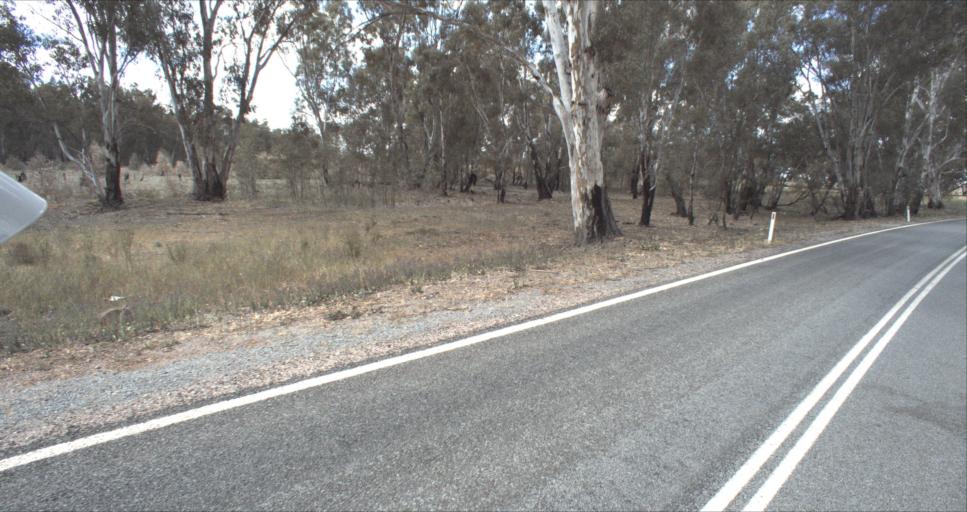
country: AU
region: New South Wales
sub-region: Leeton
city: Leeton
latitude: -34.6235
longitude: 146.3829
